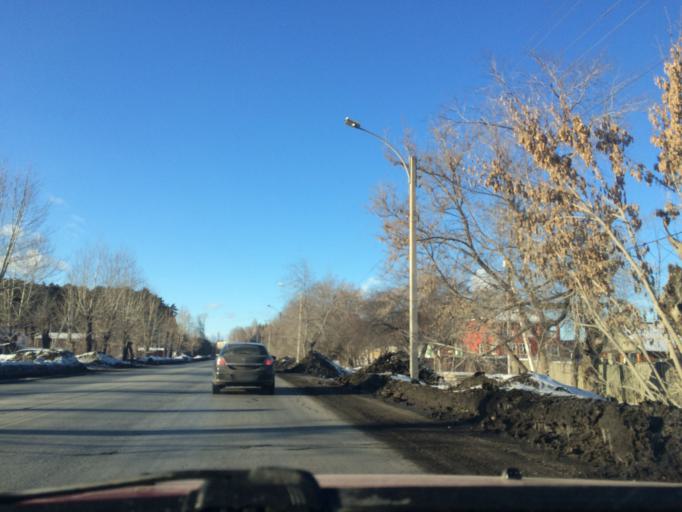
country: RU
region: Sverdlovsk
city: Istok
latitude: 56.7742
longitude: 60.8061
